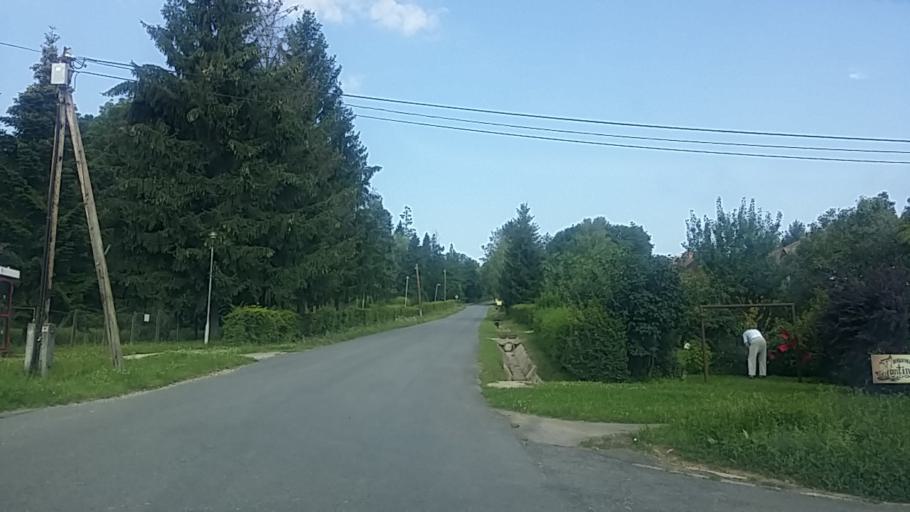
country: HU
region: Zala
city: Lenti
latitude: 46.5545
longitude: 16.5530
